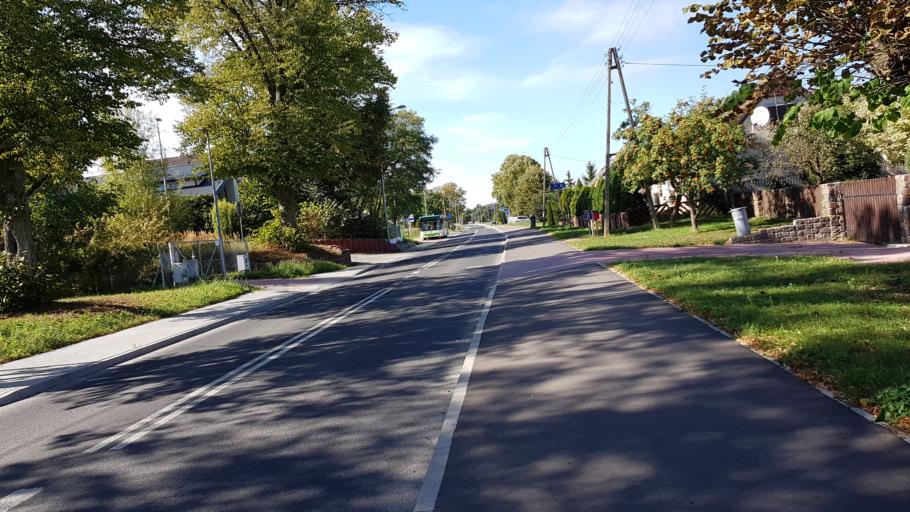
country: PL
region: West Pomeranian Voivodeship
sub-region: Powiat policki
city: Przeclaw
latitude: 53.3494
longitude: 14.4764
